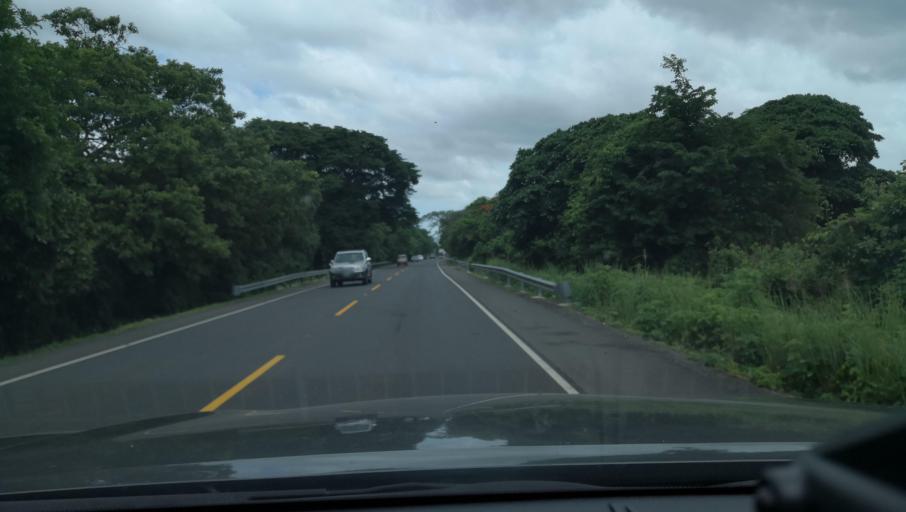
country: NI
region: Masaya
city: Nindiri
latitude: 12.0128
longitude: -86.1146
